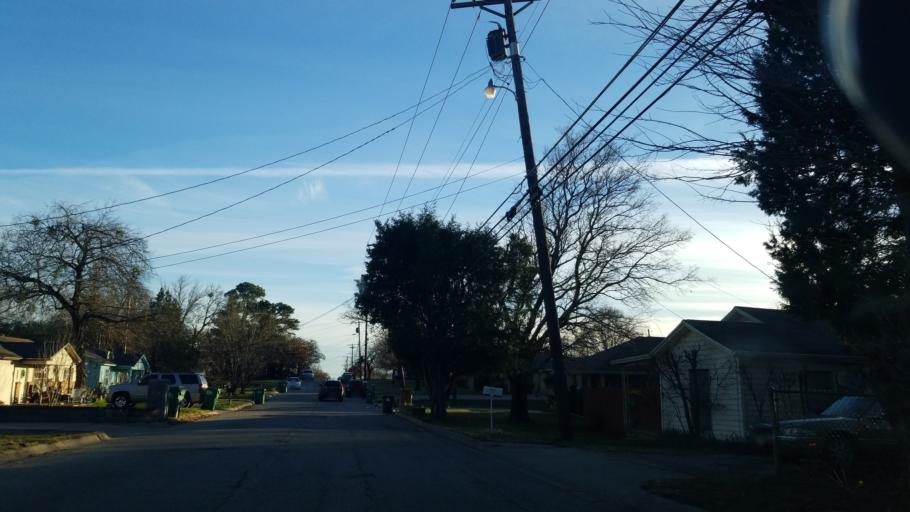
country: US
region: Texas
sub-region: Denton County
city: Denton
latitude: 33.1926
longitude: -97.1418
